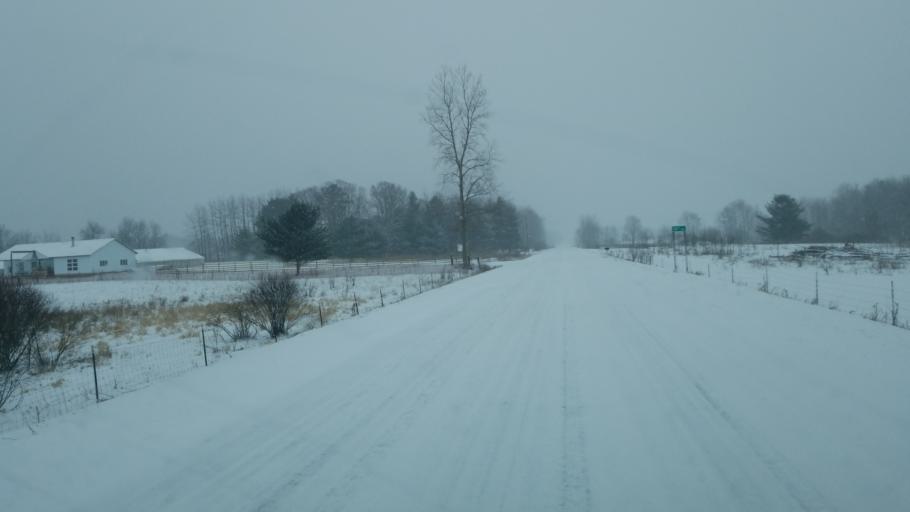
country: US
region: Michigan
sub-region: Mecosta County
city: Canadian Lakes
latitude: 43.5761
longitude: -85.3565
